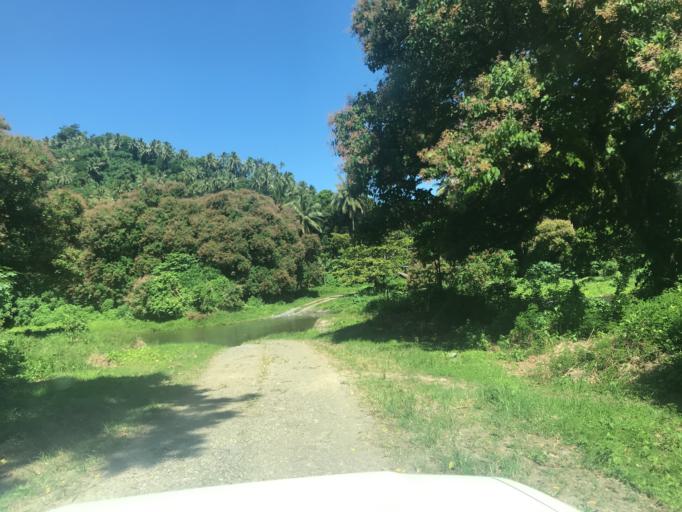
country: VU
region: Sanma
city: Luganville
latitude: -15.6067
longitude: 166.7848
